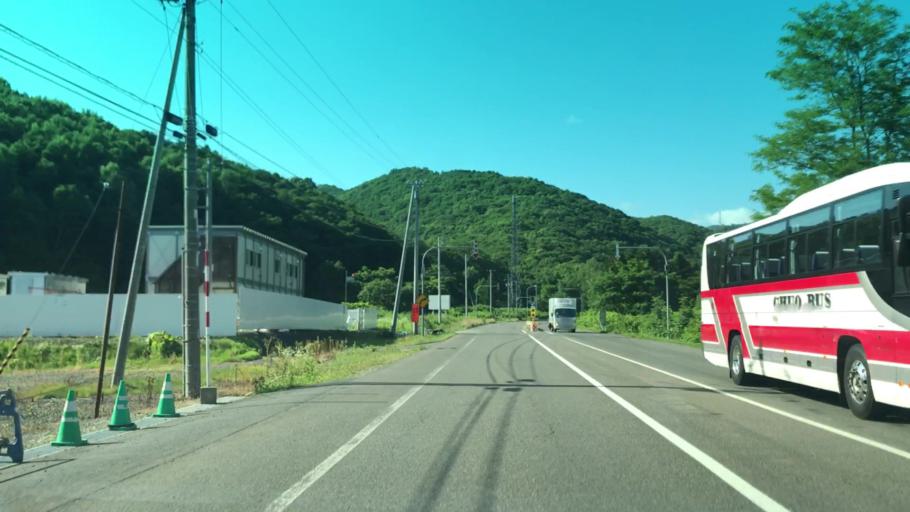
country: JP
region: Hokkaido
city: Iwanai
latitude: 43.0063
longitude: 140.6664
